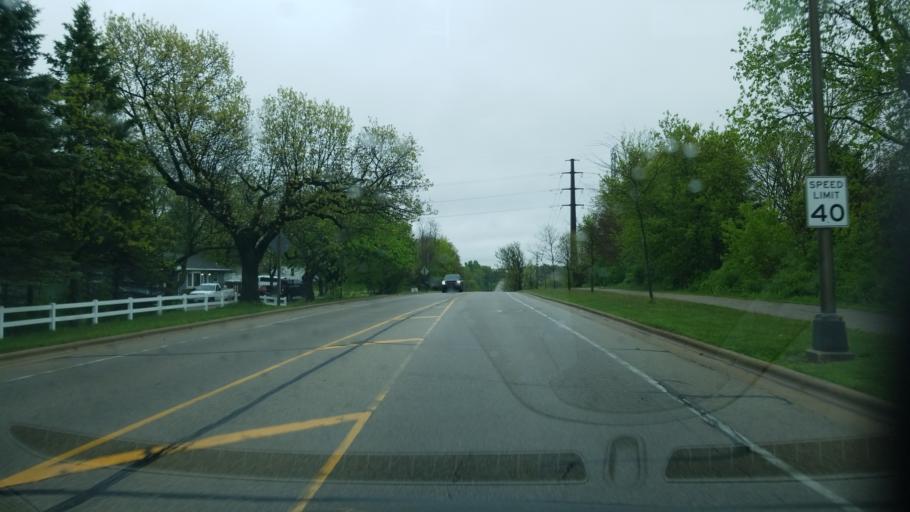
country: US
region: Wisconsin
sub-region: Dane County
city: Fitchburg
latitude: 42.9918
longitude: -89.4286
